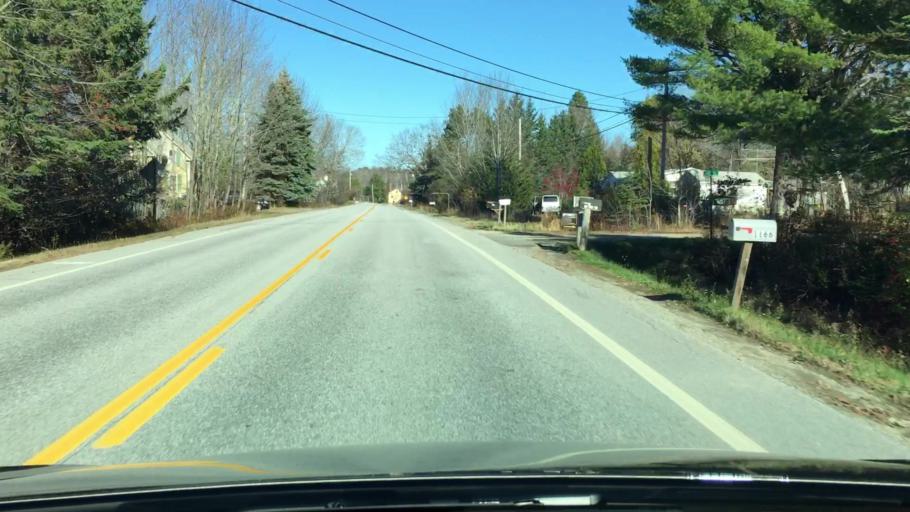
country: US
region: Maine
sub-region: Waldo County
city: Winterport
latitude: 44.6505
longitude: -68.8233
